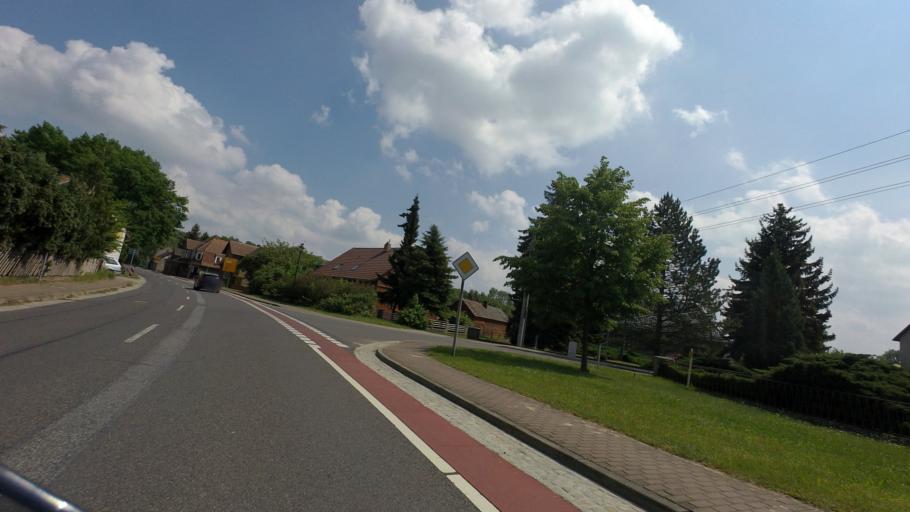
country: DE
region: Saxony
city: Schleife
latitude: 51.5456
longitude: 14.5359
